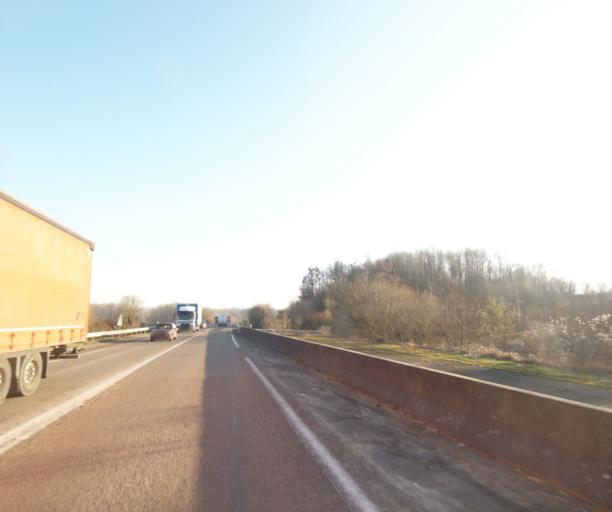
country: FR
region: Champagne-Ardenne
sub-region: Departement de la Haute-Marne
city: Chevillon
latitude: 48.5019
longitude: 5.1047
